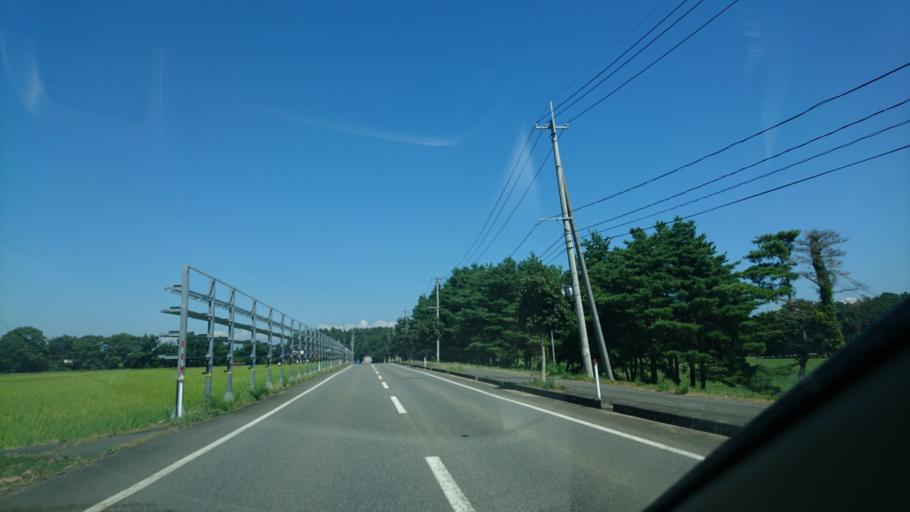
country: JP
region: Iwate
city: Kitakami
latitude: 39.2599
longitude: 141.0855
